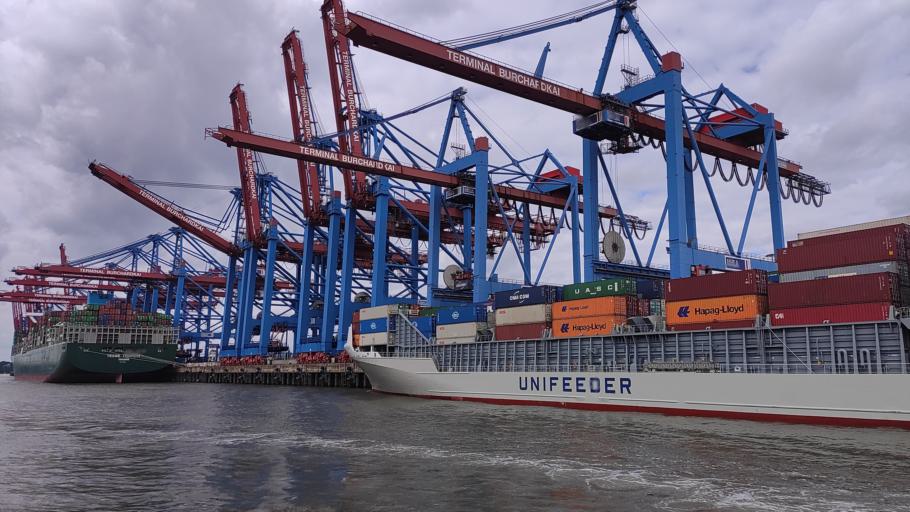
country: DE
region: Hamburg
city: Altona
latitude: 53.5267
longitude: 9.9258
